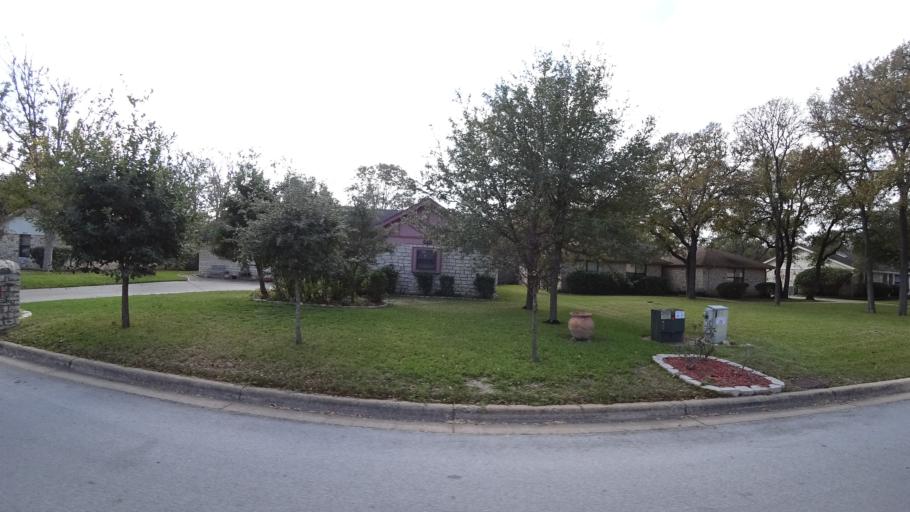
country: US
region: Texas
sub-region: Travis County
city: Shady Hollow
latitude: 30.1640
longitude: -97.8584
